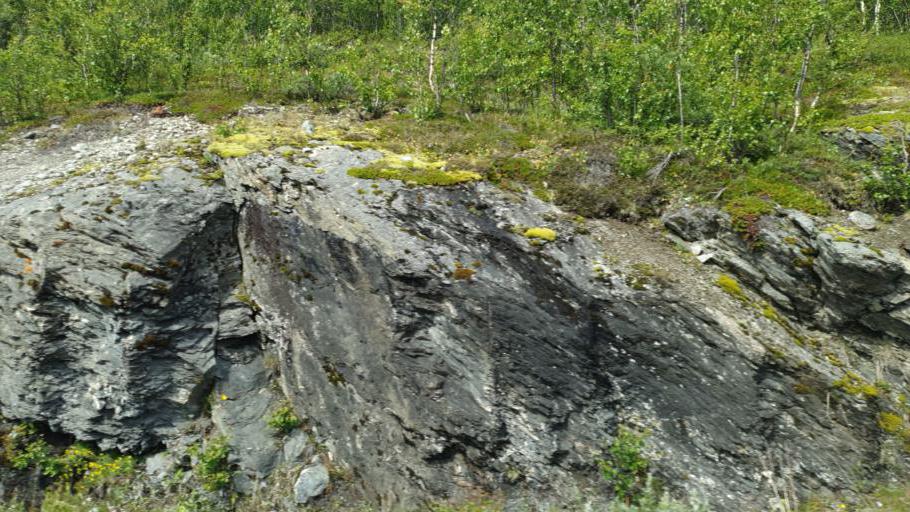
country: NO
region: Oppland
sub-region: Vaga
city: Vagamo
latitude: 61.5255
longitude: 8.8721
